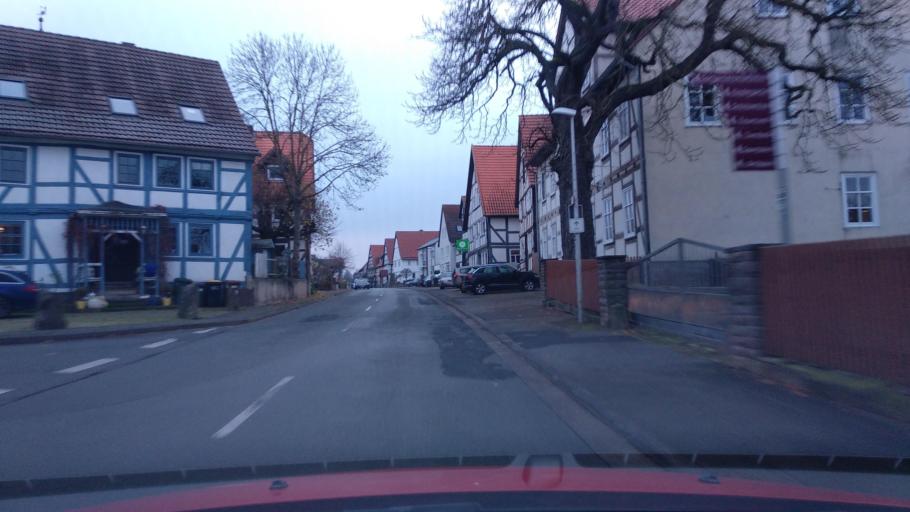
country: DE
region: Hesse
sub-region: Regierungsbezirk Kassel
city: Zierenberg
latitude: 51.4351
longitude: 9.3234
